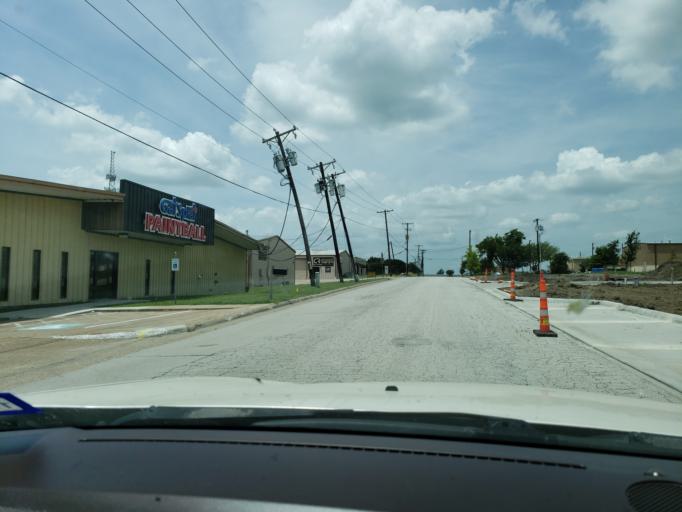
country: US
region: Texas
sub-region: Dallas County
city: Rowlett
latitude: 32.9067
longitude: -96.5573
